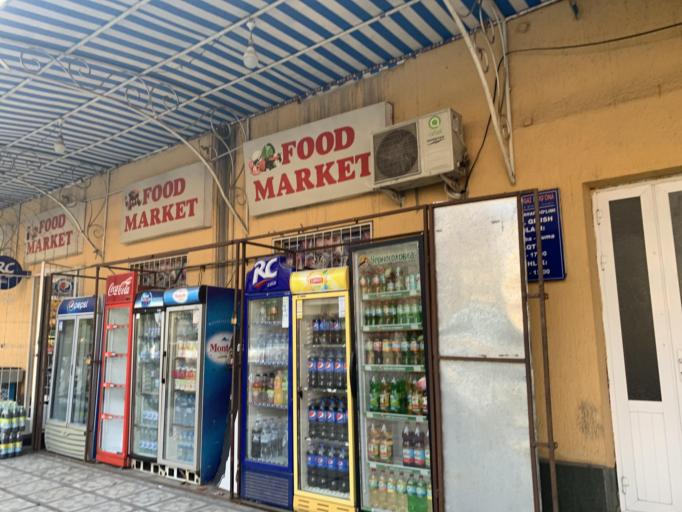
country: UZ
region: Fergana
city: Qo`qon
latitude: 40.5299
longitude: 70.9387
